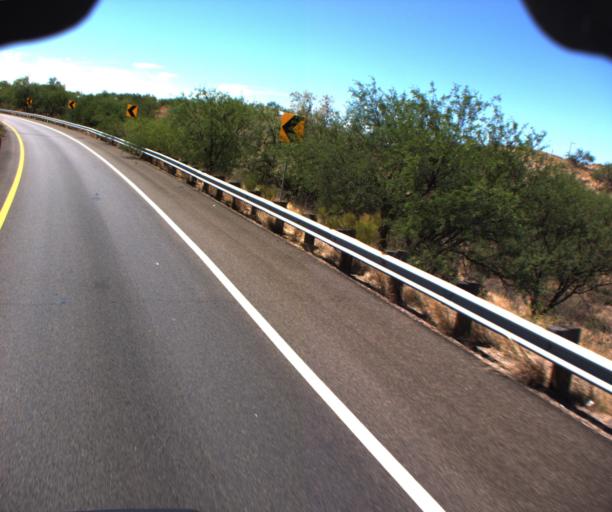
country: US
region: Arizona
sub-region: Santa Cruz County
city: Nogales
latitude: 31.3968
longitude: -110.9610
